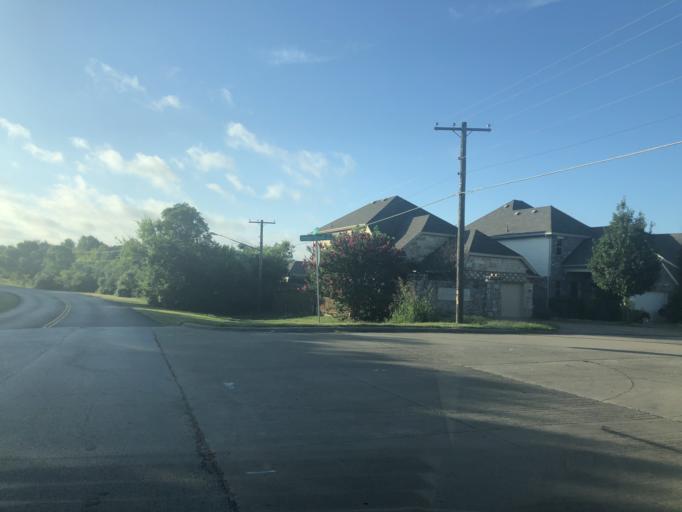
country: US
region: Texas
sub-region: Dallas County
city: Duncanville
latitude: 32.6655
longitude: -96.9511
